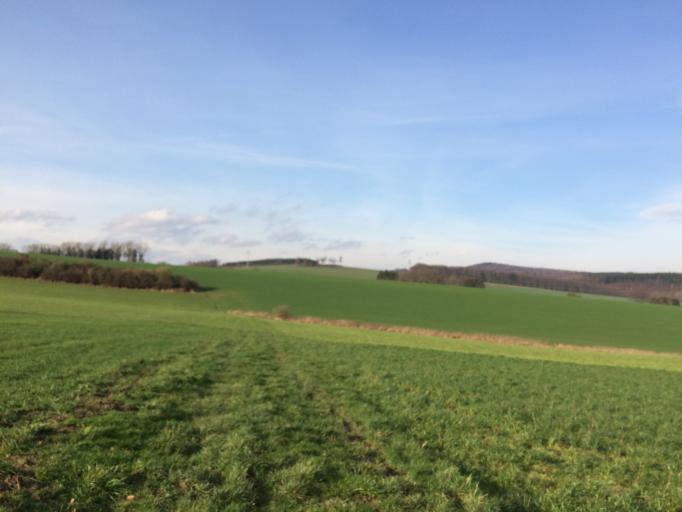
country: DE
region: North Rhine-Westphalia
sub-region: Regierungsbezirk Detmold
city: Blomberg
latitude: 51.9194
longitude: 9.1346
